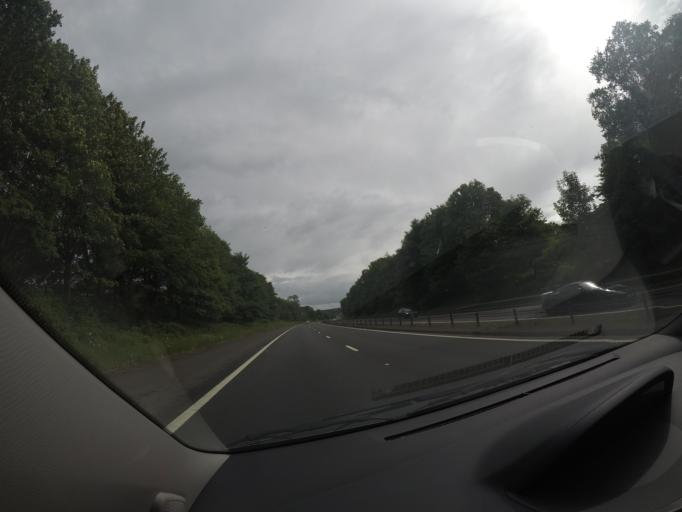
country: GB
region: Scotland
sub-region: Falkirk
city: Dunipace
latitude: 56.0436
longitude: -3.9174
